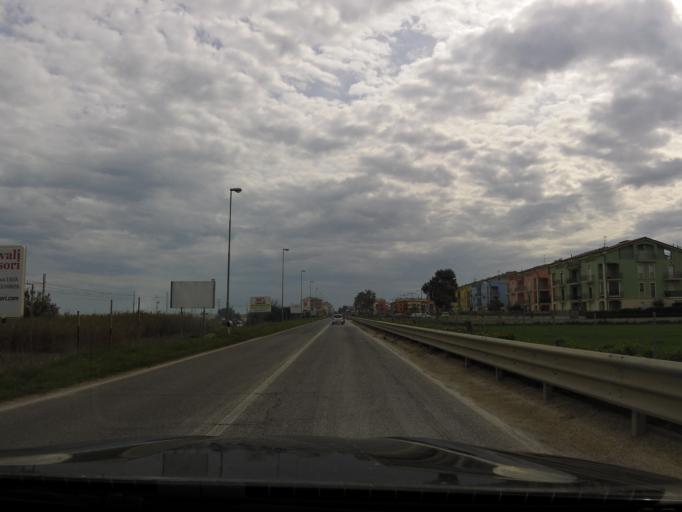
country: IT
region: The Marches
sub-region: Provincia di Macerata
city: Porto Potenza Picena
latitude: 43.3765
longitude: 13.6903
